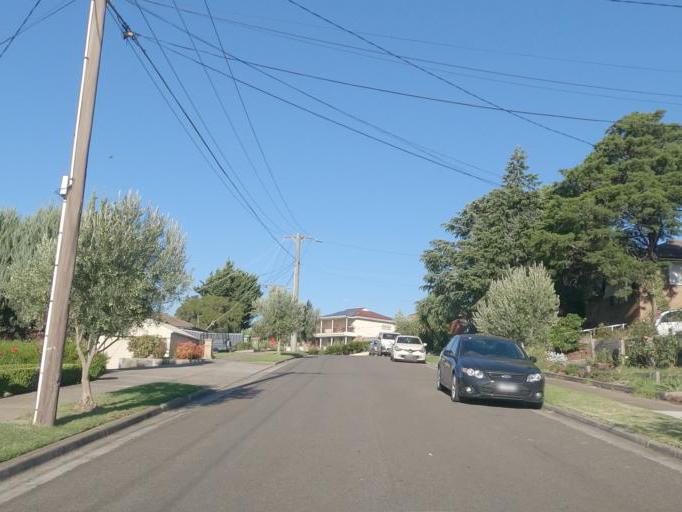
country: AU
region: Victoria
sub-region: Hume
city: Gladstone Park
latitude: -37.6837
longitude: 144.8972
